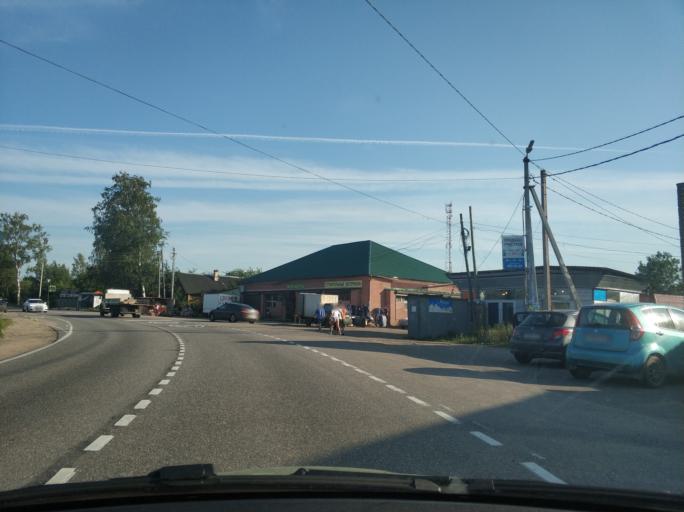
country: RU
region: Leningrad
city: Borisova Griva
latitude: 60.0886
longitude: 31.0188
